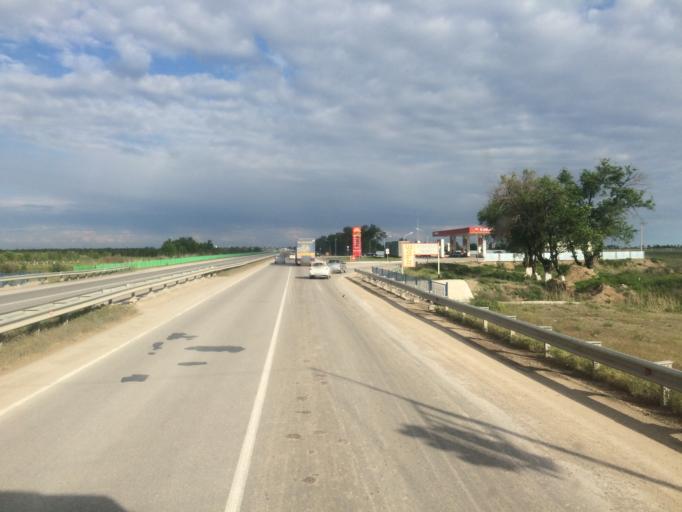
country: KZ
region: Ongtustik Qazaqstan
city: Turkestan
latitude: 43.2705
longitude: 68.3490
